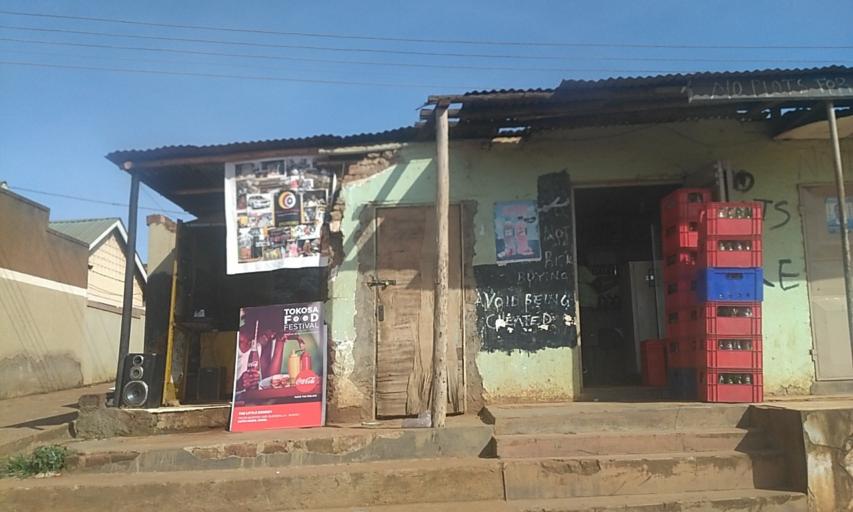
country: UG
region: Central Region
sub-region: Wakiso District
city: Kireka
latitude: 0.3655
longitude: 32.6244
